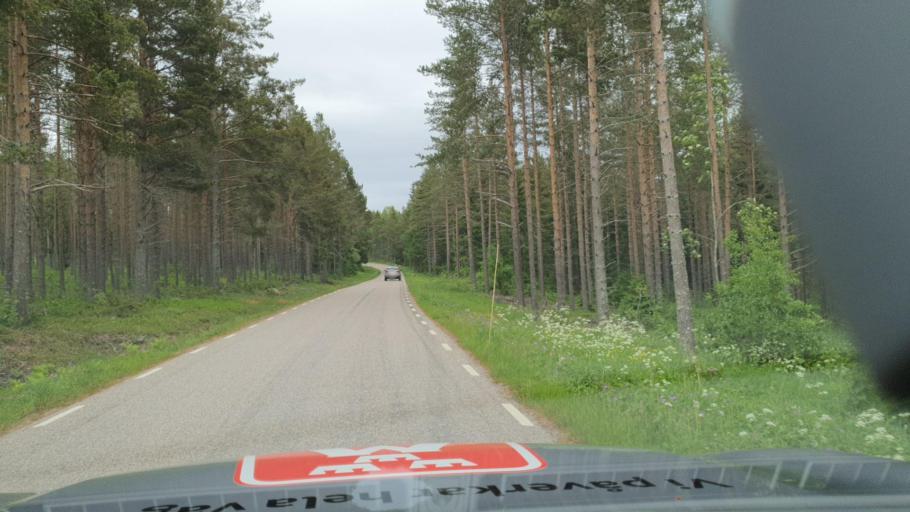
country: SE
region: Vaesternorrland
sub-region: Kramfors Kommun
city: Nordingra
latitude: 62.8669
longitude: 18.3695
